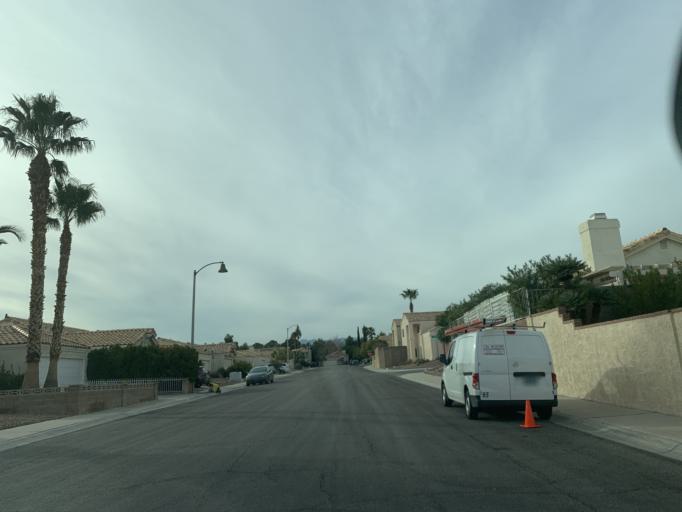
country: US
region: Nevada
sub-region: Clark County
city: Summerlin South
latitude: 36.1418
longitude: -115.3034
